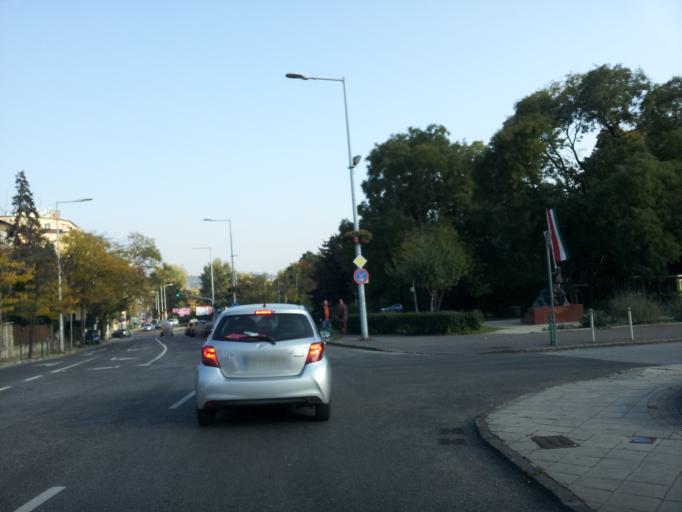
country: HU
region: Budapest
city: Budapest XII. keruelet
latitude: 47.4908
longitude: 19.0147
